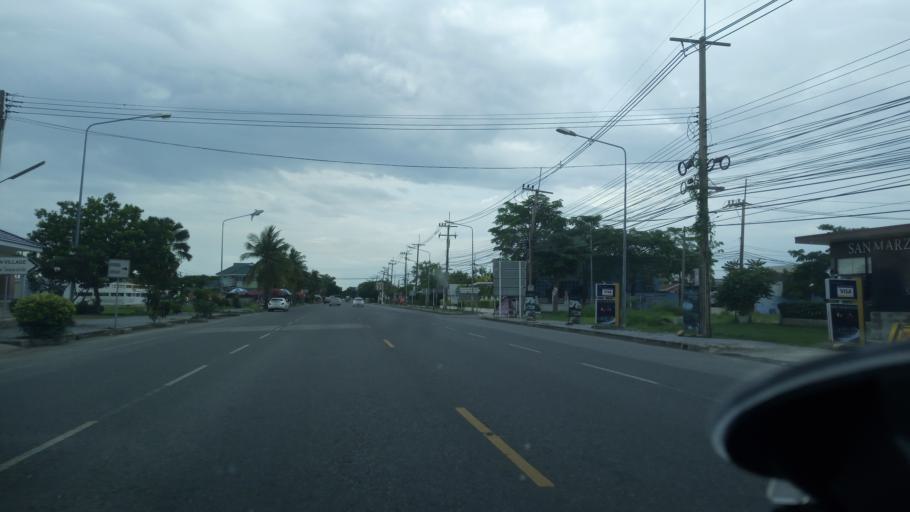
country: TH
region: Chon Buri
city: Chon Buri
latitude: 13.3097
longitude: 100.9117
